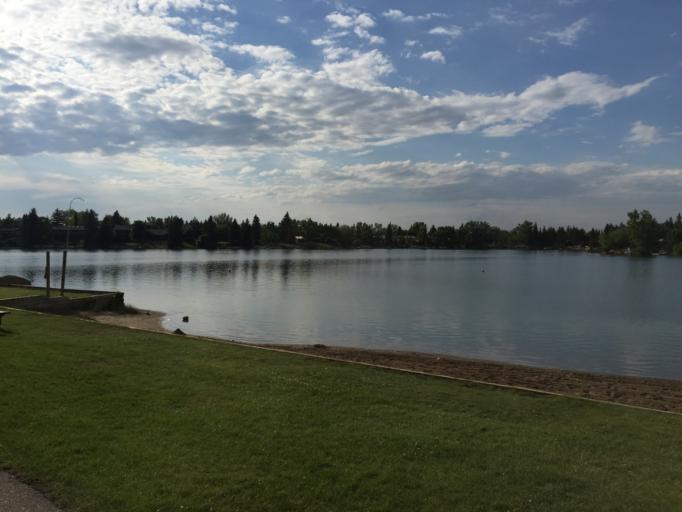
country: CA
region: Alberta
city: Calgary
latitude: 50.9414
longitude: -114.0502
